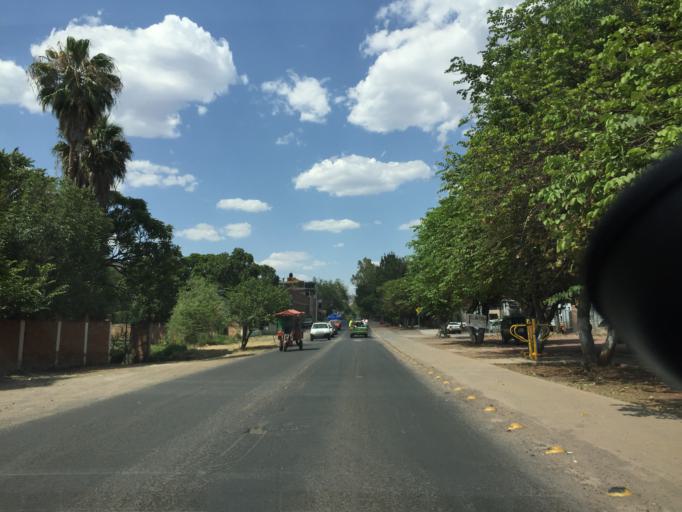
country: MX
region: Jalisco
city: Atotonilco el Alto
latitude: 20.5523
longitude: -102.4982
